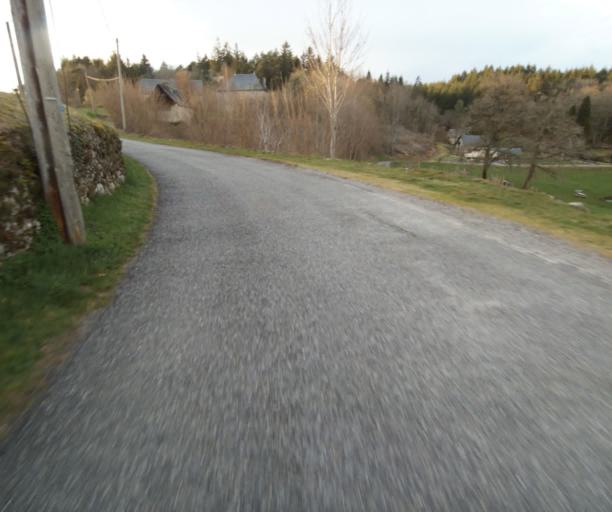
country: FR
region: Limousin
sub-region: Departement de la Correze
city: Argentat
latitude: 45.2466
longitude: 1.9815
